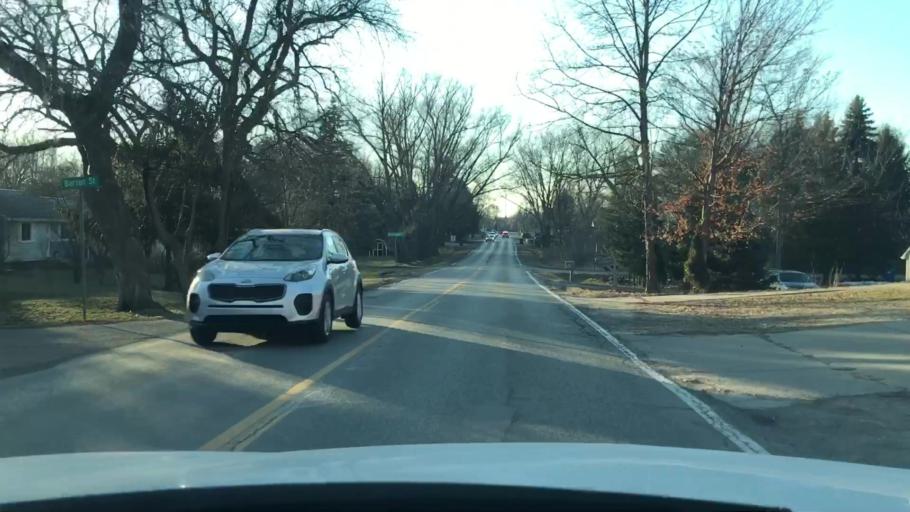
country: US
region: Michigan
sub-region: Oakland County
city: Wolverine Lake
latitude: 42.5989
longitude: -83.4418
